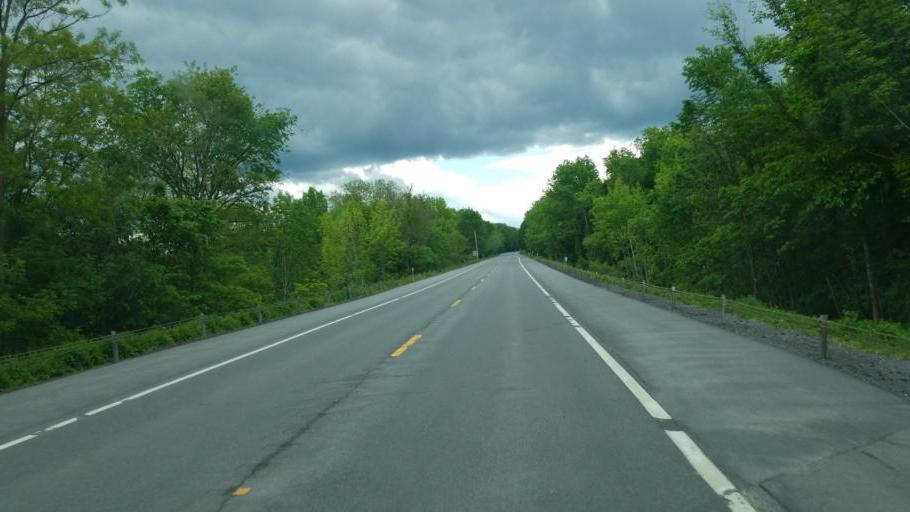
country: US
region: New York
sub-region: Oneida County
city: Chadwicks
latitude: 42.9783
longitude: -75.2529
